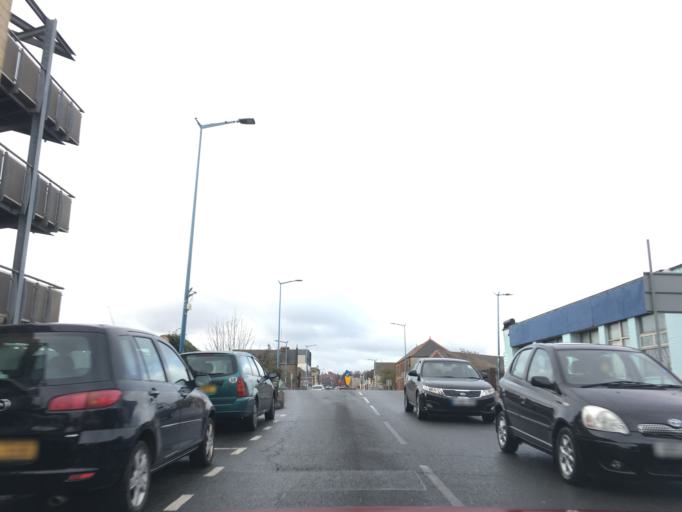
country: GB
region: Wales
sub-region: Cardiff
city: Cardiff
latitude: 51.4935
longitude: -3.1738
